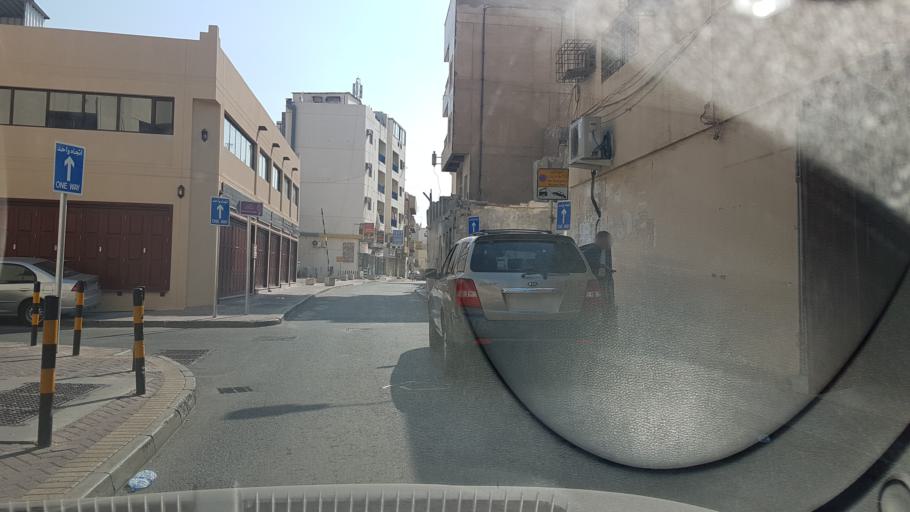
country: BH
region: Manama
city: Manama
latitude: 26.2351
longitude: 50.5797
